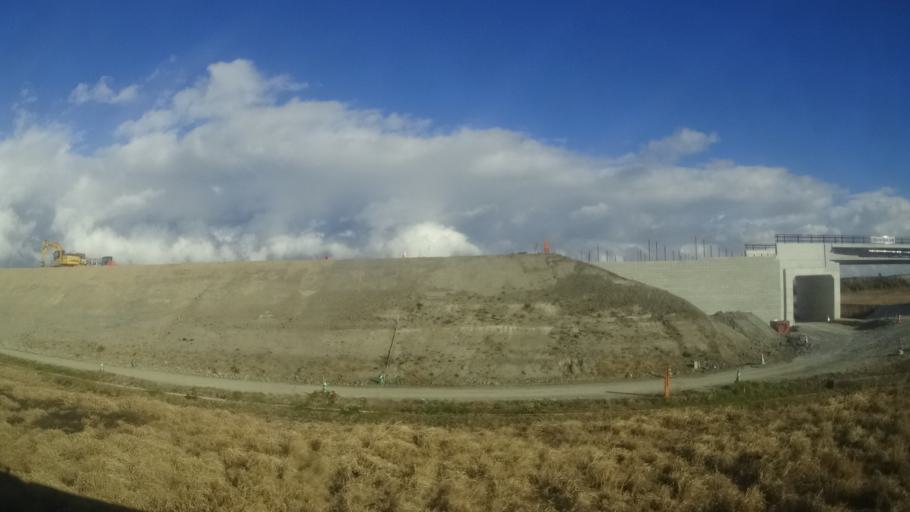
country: JP
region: Miyagi
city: Marumori
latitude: 37.8755
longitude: 140.9270
